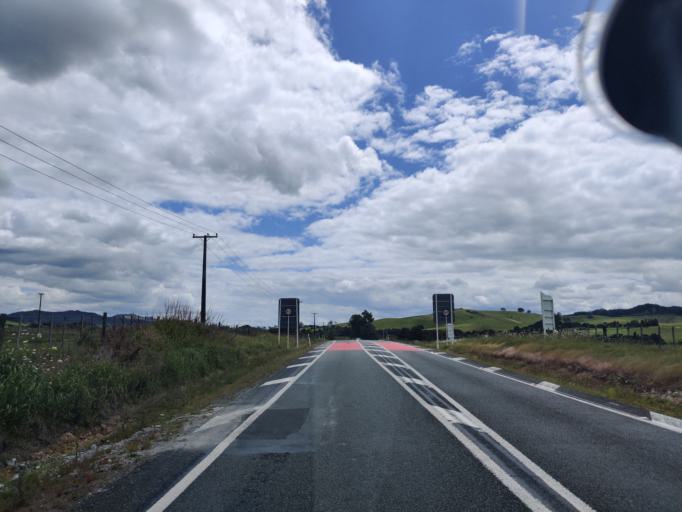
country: NZ
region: Northland
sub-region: Far North District
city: Paihia
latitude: -35.2812
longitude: 174.0424
